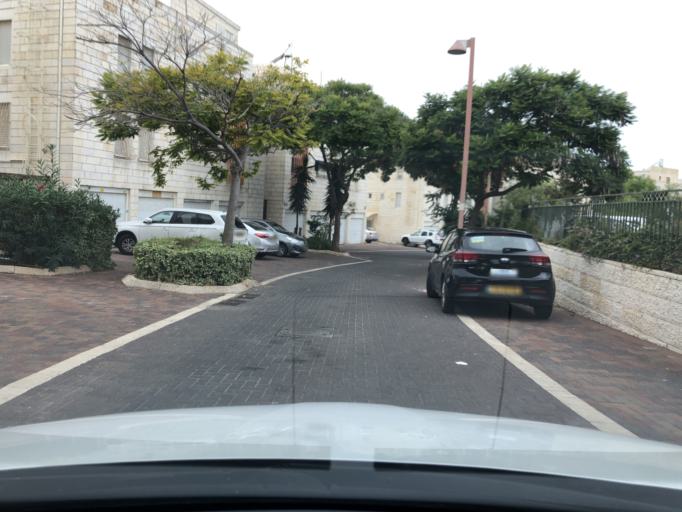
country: IL
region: Central District
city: Modiin
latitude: 31.9070
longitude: 35.0090
